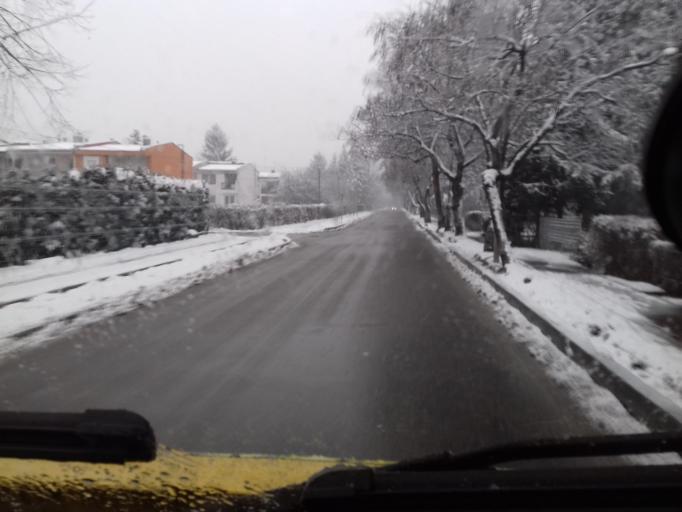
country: BA
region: Federation of Bosnia and Herzegovina
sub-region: Kanton Sarajevo
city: Sarajevo
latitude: 43.8272
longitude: 18.2978
